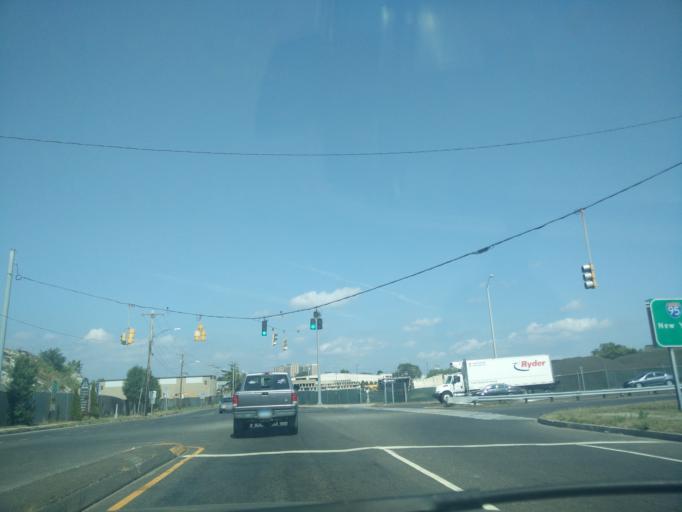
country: US
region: Connecticut
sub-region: Fairfield County
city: Bridgeport
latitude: 41.1786
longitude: -73.1730
